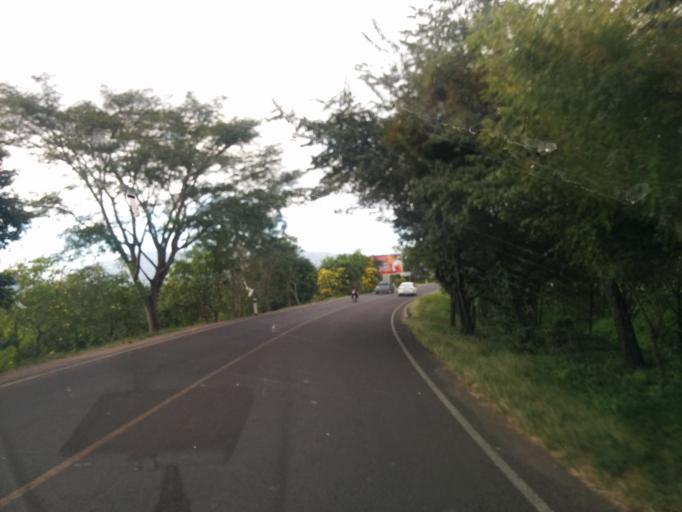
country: NI
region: Esteli
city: Esteli
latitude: 13.0612
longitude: -86.3448
